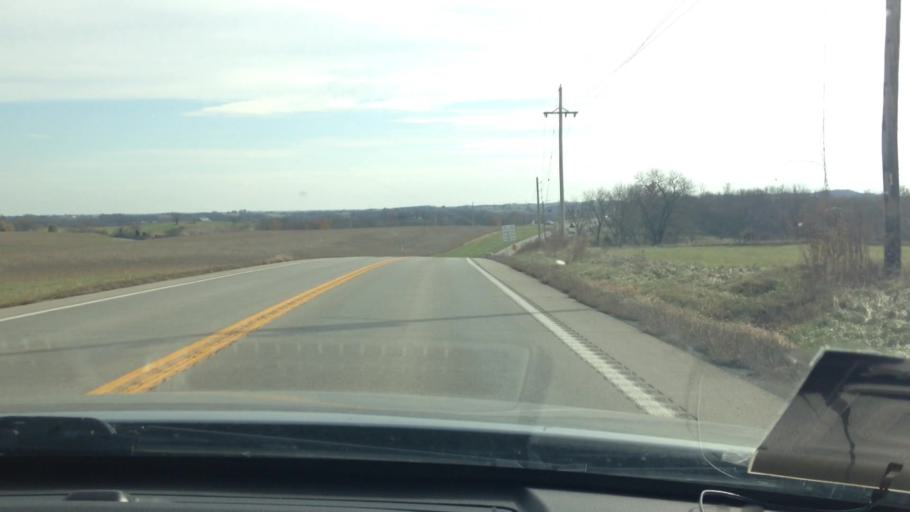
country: US
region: Missouri
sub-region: Platte County
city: Weston
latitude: 39.4031
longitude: -94.8641
